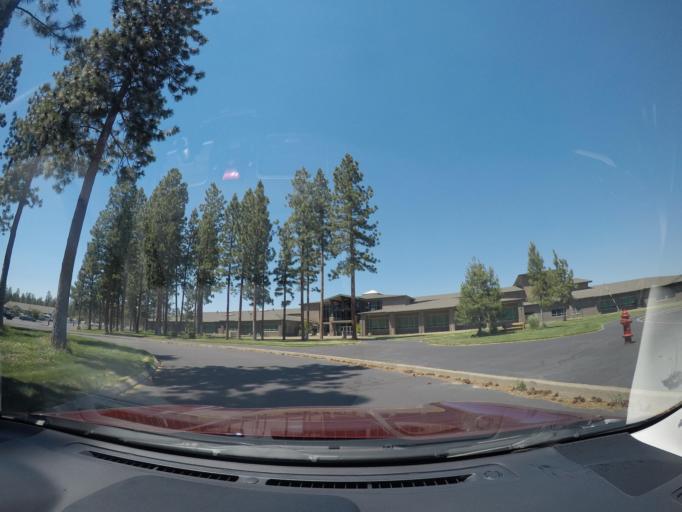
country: US
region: Oregon
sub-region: Deschutes County
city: Sisters
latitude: 44.2954
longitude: -121.5756
